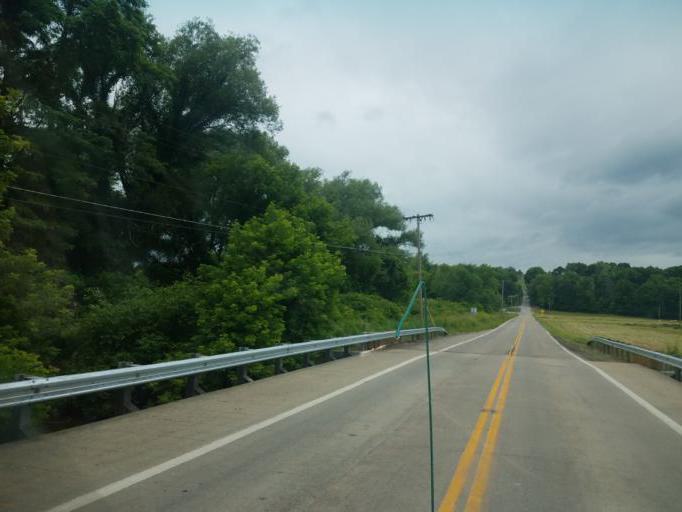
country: US
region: Ohio
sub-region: Columbiana County
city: Leetonia
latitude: 40.8576
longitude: -80.7966
